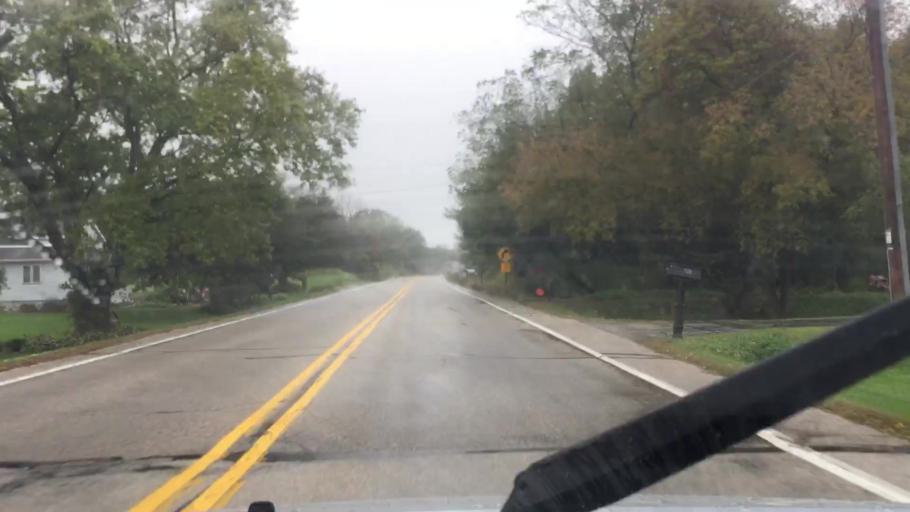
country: US
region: Wisconsin
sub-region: Waukesha County
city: Eagle
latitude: 42.8790
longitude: -88.4792
